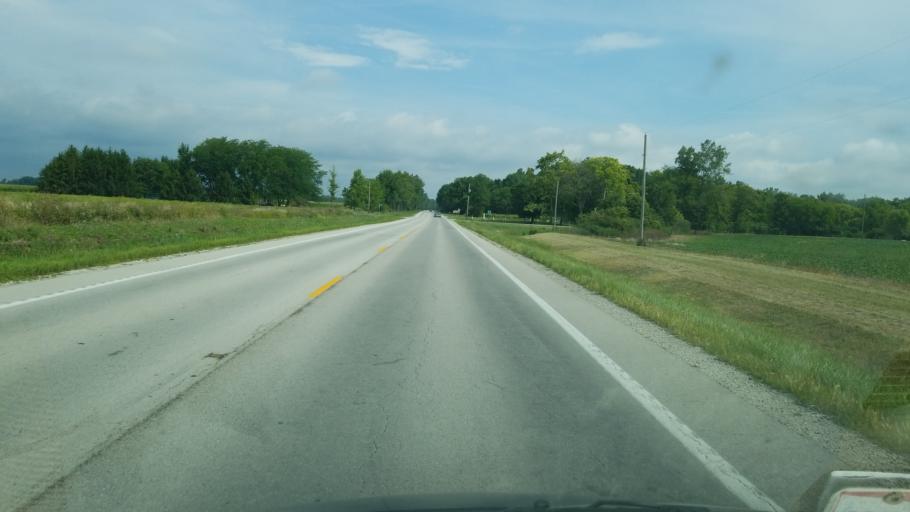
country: US
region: Ohio
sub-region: Sandusky County
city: Ballville
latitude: 41.2612
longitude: -83.1679
